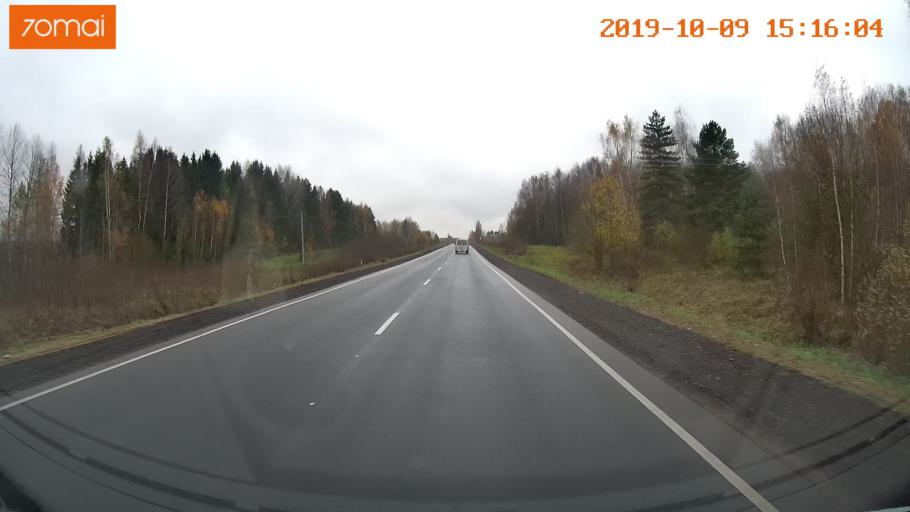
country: RU
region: Kostroma
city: Susanino
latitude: 58.1143
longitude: 41.5871
